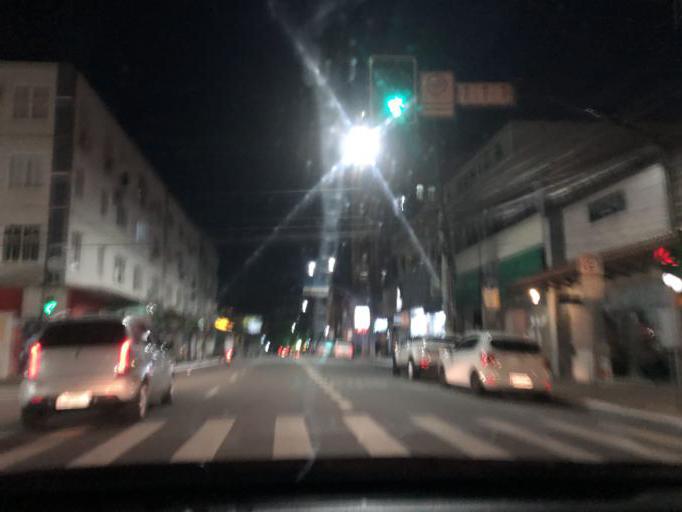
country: BR
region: Santa Catarina
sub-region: Jaragua Do Sul
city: Jaragua do Sul
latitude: -26.4890
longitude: -49.0828
